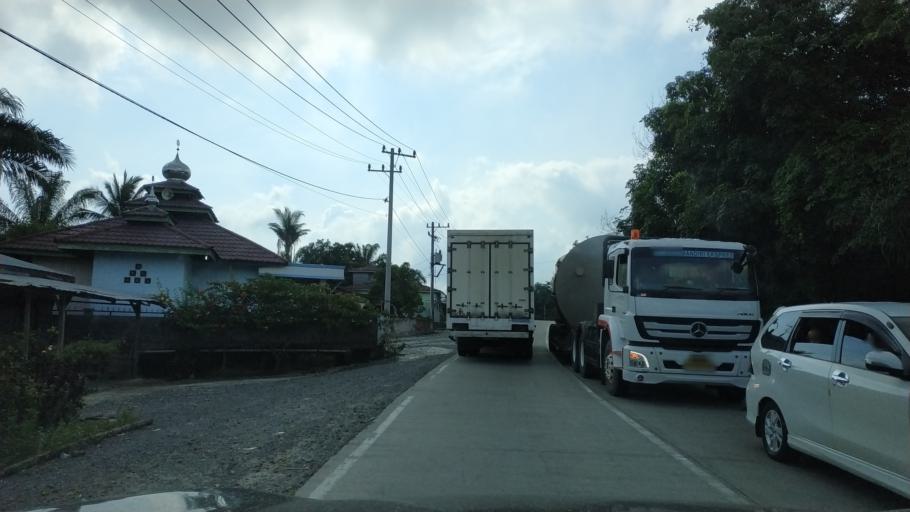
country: ID
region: Riau
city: Pangkalan Kasai
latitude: -0.6969
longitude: 102.4887
